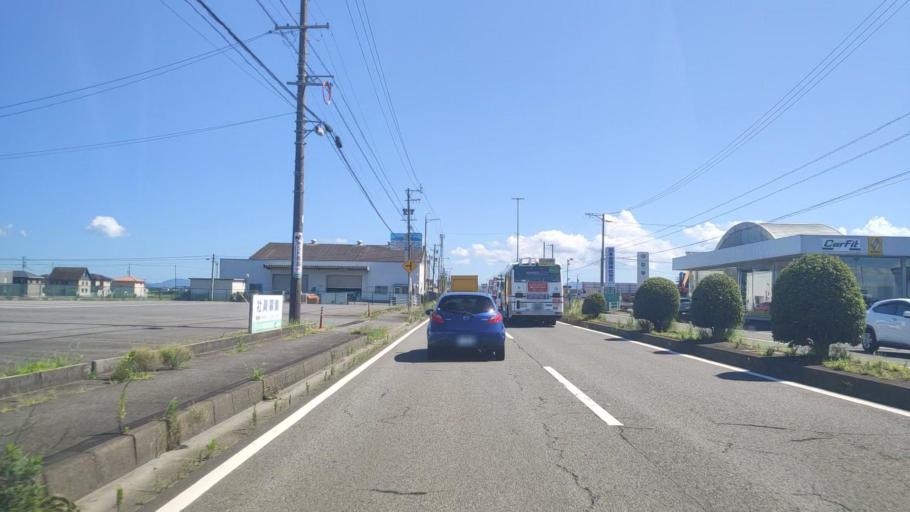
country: JP
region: Mie
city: Hisai-motomachi
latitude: 34.6392
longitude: 136.5181
